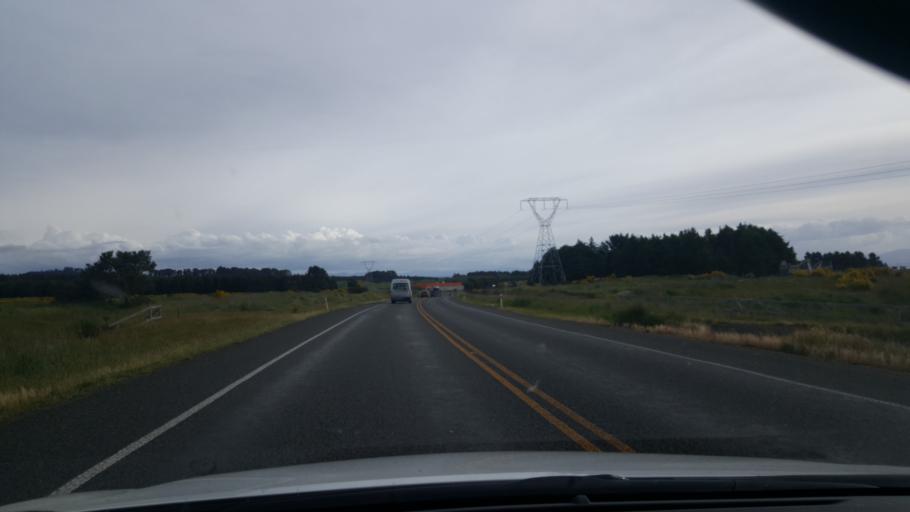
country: NZ
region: Waikato
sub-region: Taupo District
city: Taupo
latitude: -38.6947
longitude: 176.1137
